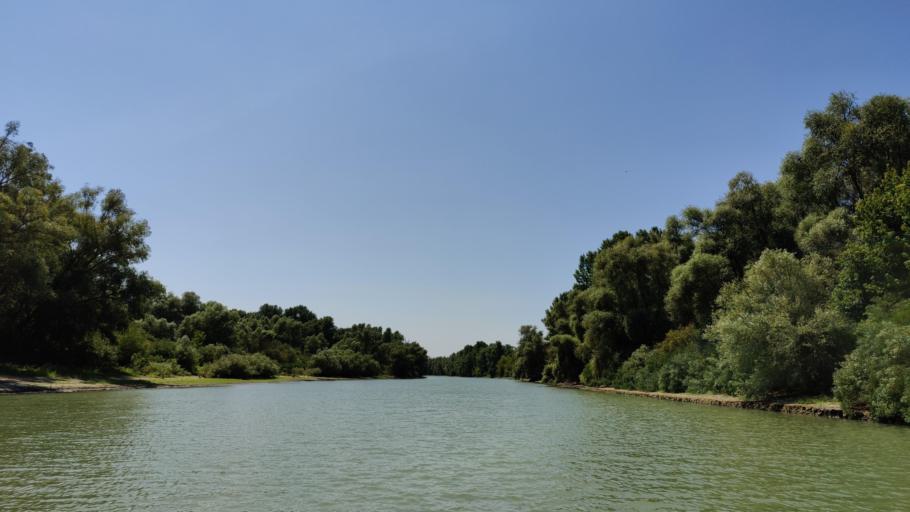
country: RO
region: Tulcea
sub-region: Municipiul Tulcea
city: Tulcea
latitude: 45.2115
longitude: 28.8615
